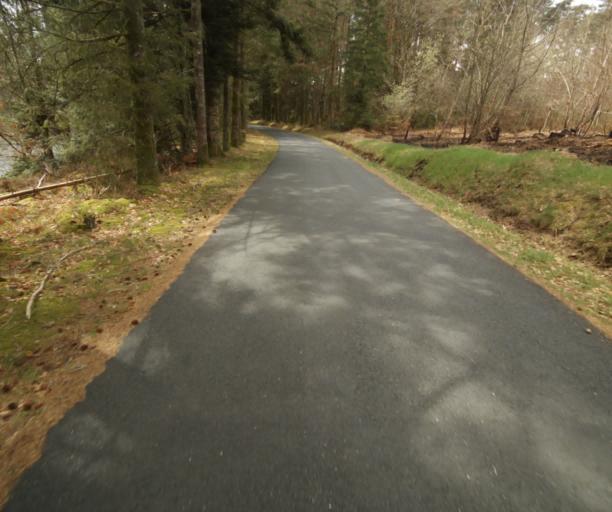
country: FR
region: Limousin
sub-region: Departement de la Correze
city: Correze
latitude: 45.3404
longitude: 1.9499
